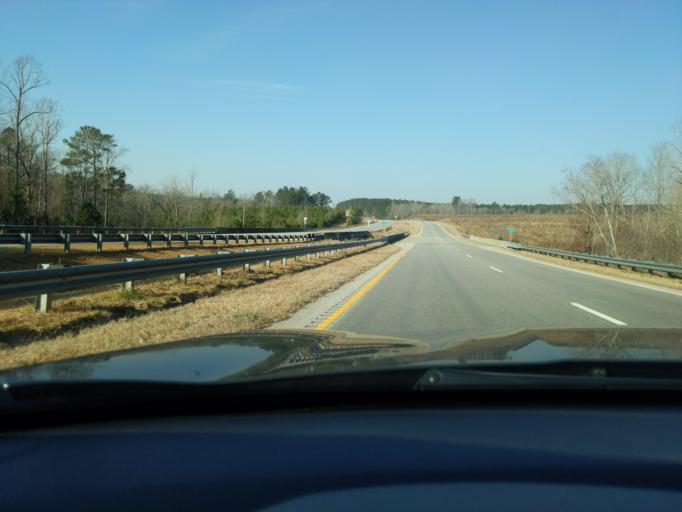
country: US
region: South Carolina
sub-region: Abbeville County
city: Abbeville
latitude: 34.1132
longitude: -82.4767
